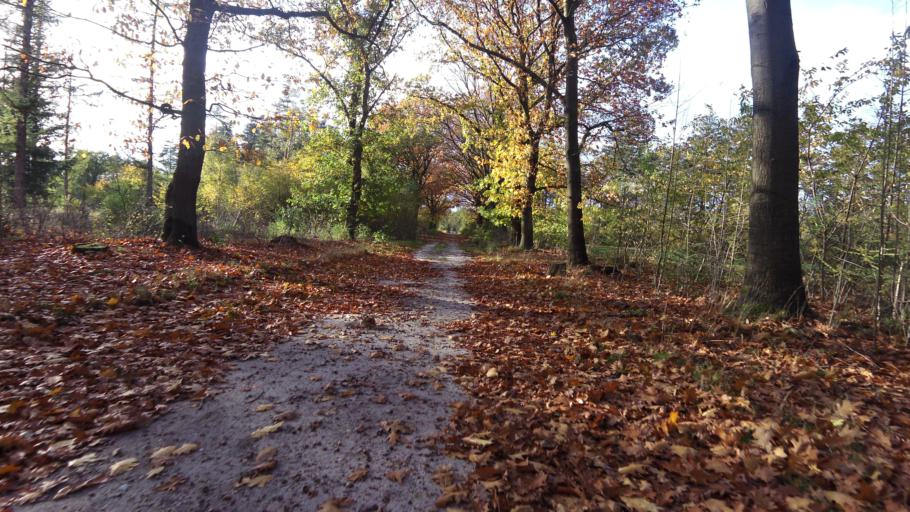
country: NL
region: Gelderland
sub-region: Gemeente Hattem
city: Hattem
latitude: 52.4384
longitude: 6.0364
